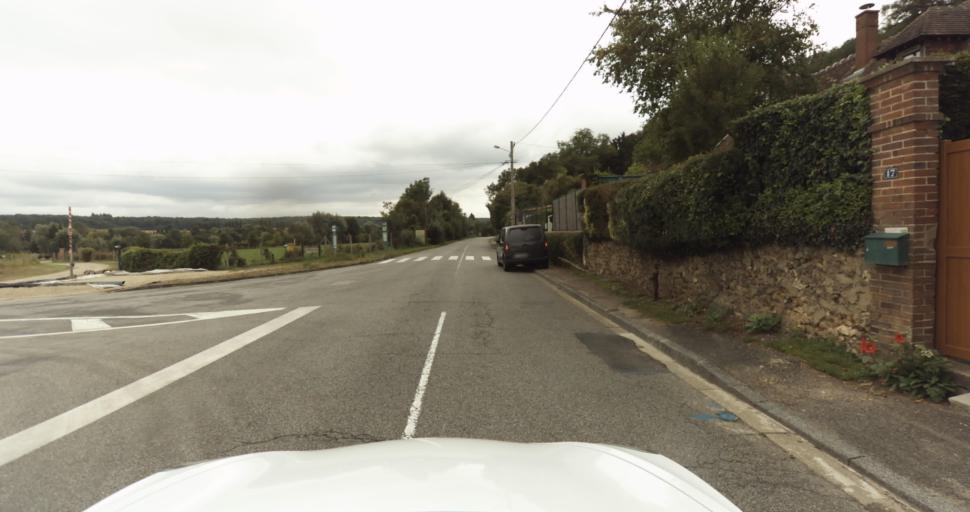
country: FR
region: Haute-Normandie
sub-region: Departement de l'Eure
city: Arnieres-sur-Iton
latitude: 49.0026
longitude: 1.0988
